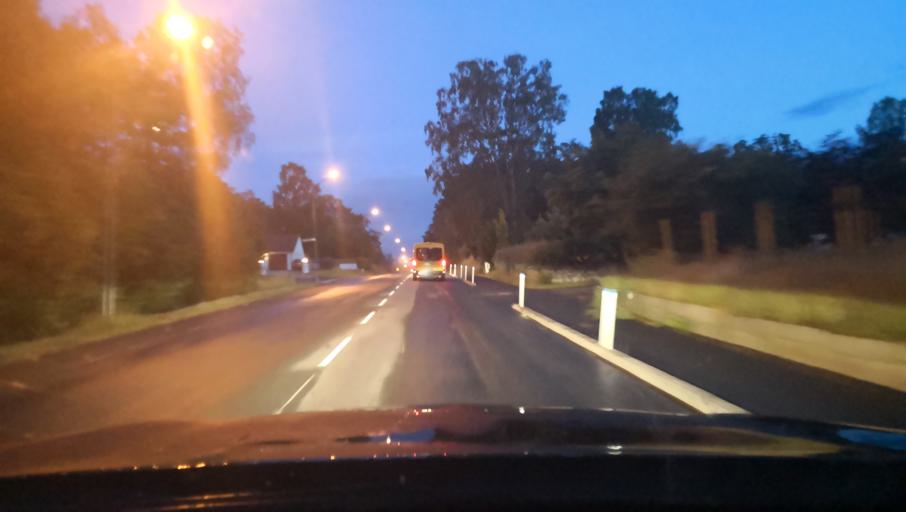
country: SE
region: Skane
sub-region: Osby Kommun
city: Osby
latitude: 56.3655
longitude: 13.9819
